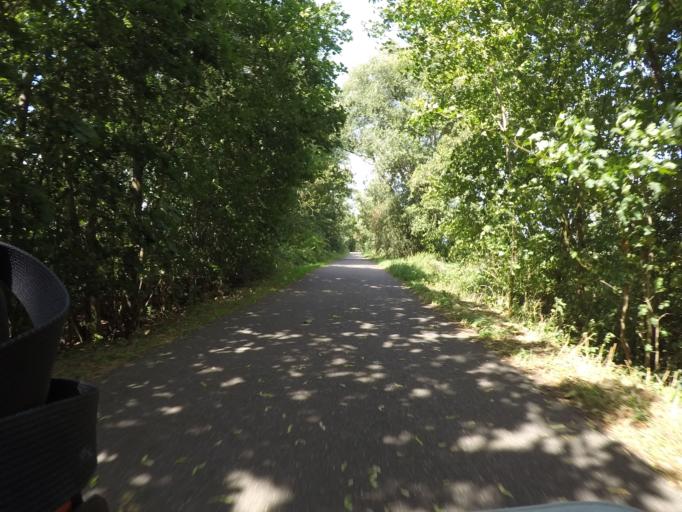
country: DE
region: Lower Saxony
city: Stelle
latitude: 53.4335
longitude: 10.1418
